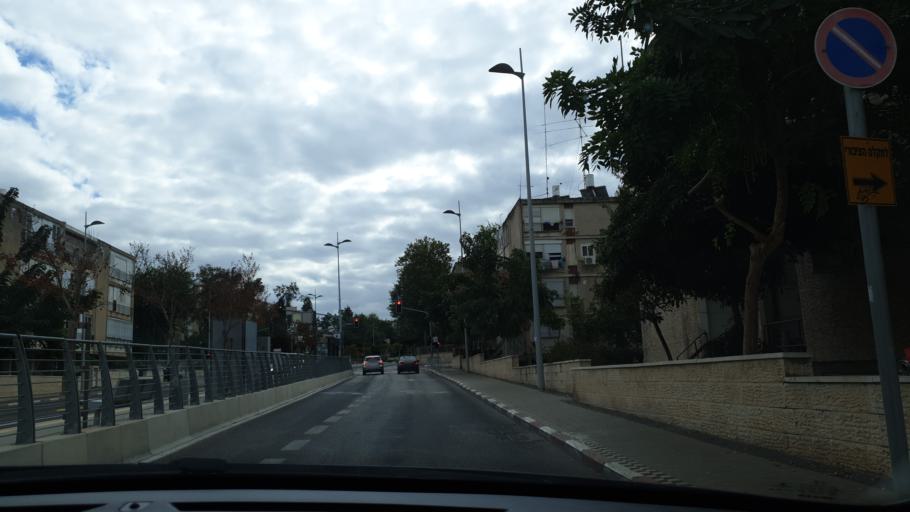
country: IL
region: Haifa
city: Qiryat Ata
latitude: 32.8142
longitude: 35.1138
